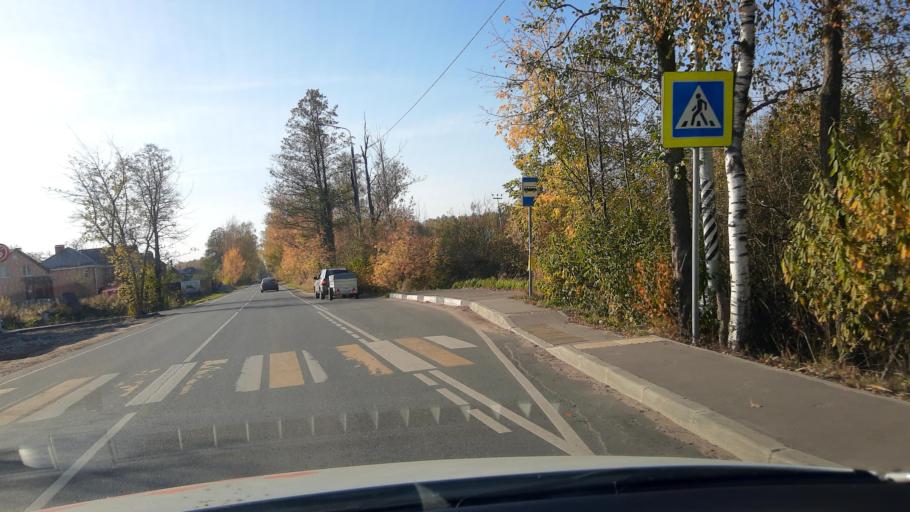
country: RU
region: Moskovskaya
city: Elektrostal'
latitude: 55.8006
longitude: 38.3850
